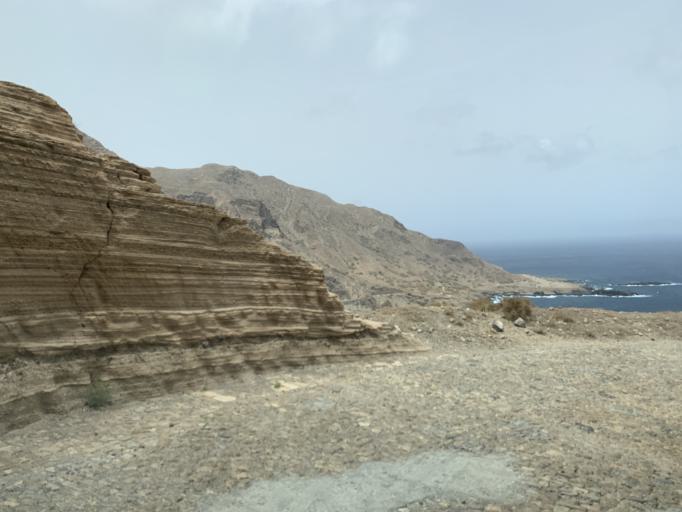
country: CV
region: Brava
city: Vila Nova Sintra
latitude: 14.8766
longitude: -24.7310
